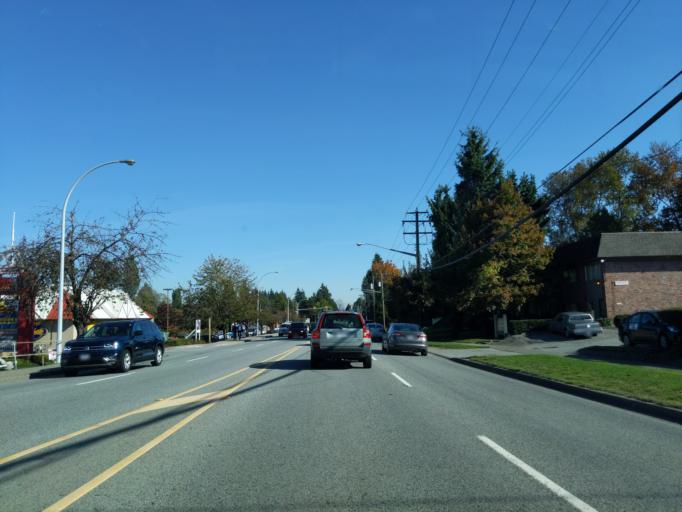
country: CA
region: British Columbia
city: Surrey
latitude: 49.1987
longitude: -122.8110
